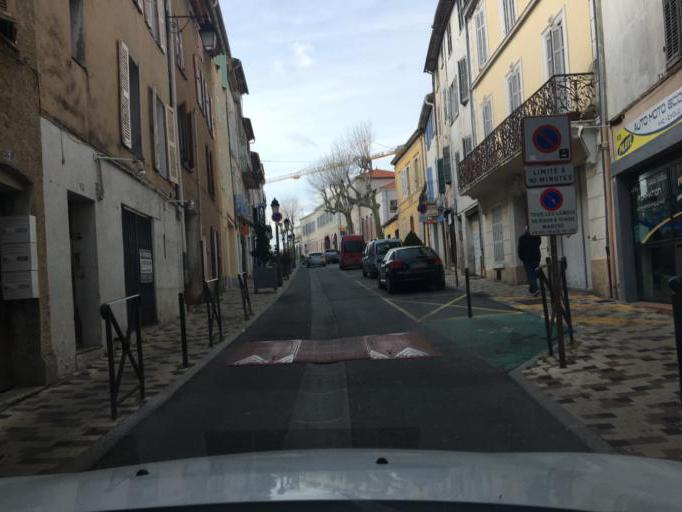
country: FR
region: Provence-Alpes-Cote d'Azur
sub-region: Departement du Var
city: Flayosc
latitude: 43.5342
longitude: 6.3960
